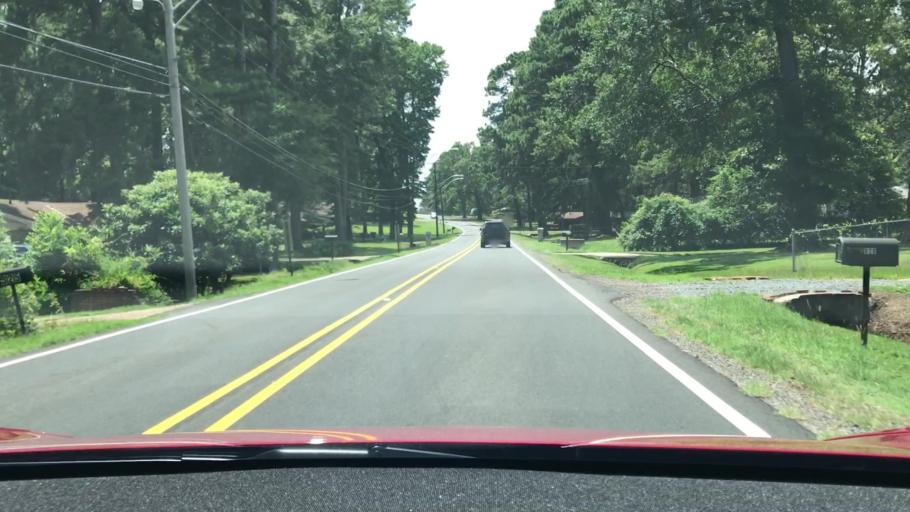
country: US
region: Louisiana
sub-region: De Soto Parish
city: Stonewall
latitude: 32.3913
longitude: -93.7753
